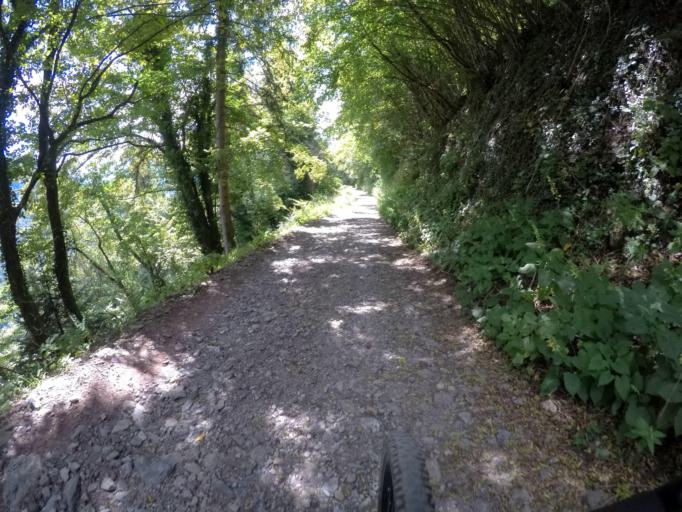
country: IT
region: Friuli Venezia Giulia
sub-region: Provincia di Udine
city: Zuglio
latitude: 46.4686
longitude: 13.0478
